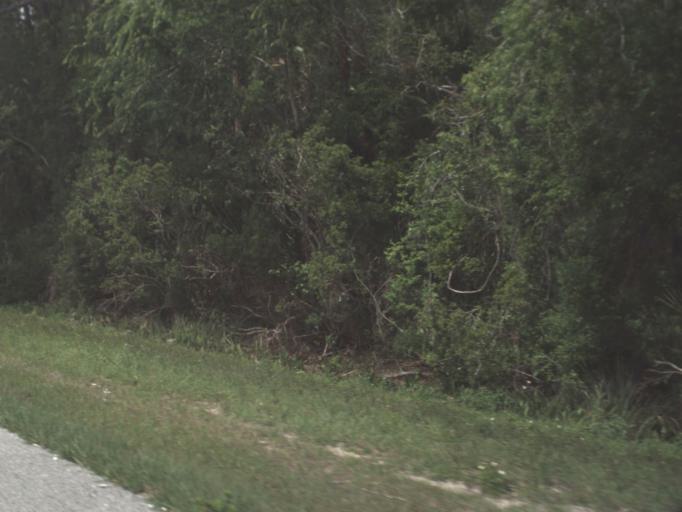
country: US
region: Florida
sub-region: Lake County
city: Lake Mack-Forest Hills
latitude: 28.9828
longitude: -81.4018
